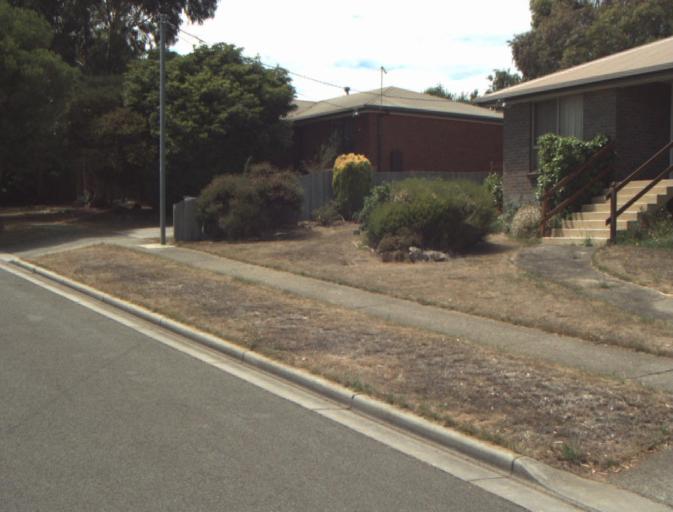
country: AU
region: Tasmania
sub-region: Launceston
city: Mayfield
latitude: -41.3791
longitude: 147.1163
